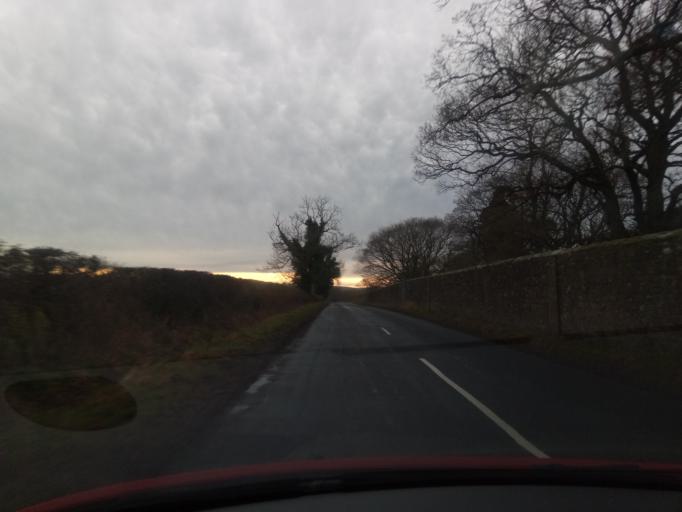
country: GB
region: England
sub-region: Northumberland
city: Alnwick
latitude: 55.4277
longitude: -1.7138
